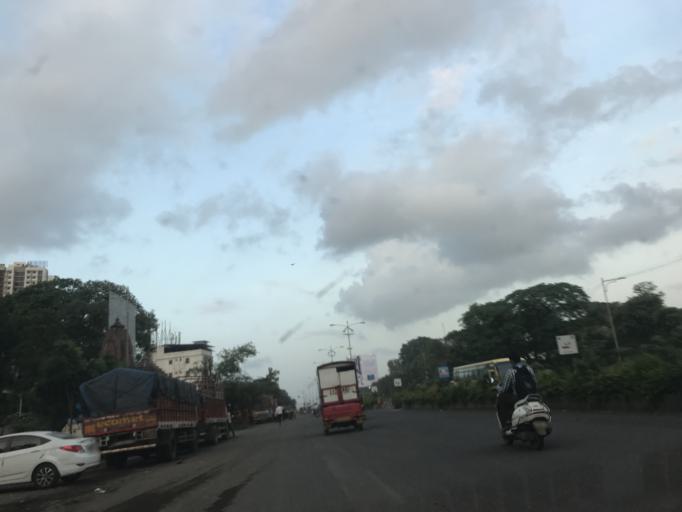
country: IN
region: Maharashtra
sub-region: Thane
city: Thane
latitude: 19.2199
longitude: 72.9864
